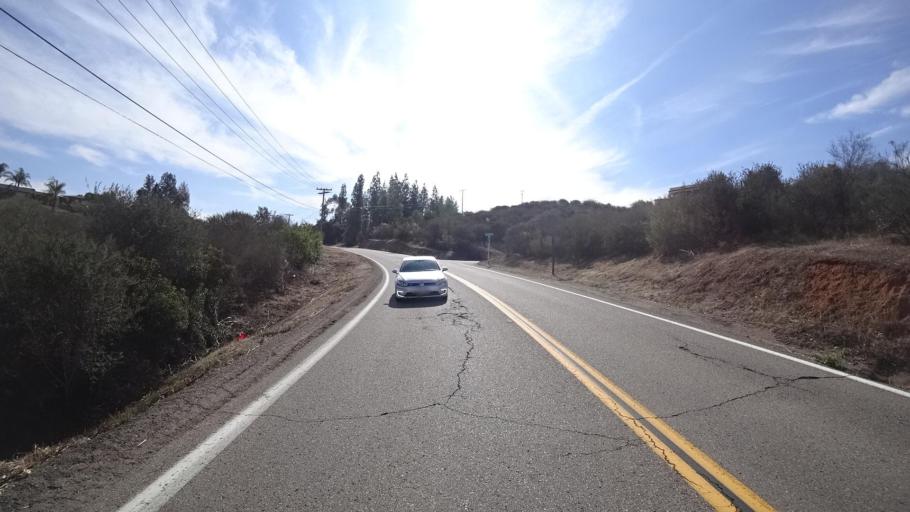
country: US
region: California
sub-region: San Diego County
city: Harbison Canyon
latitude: 32.8371
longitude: -116.8030
